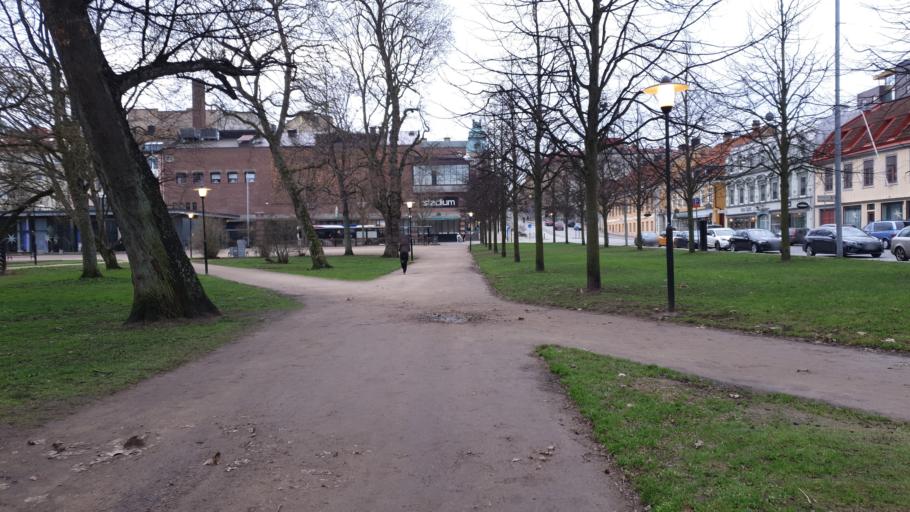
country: SE
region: Blekinge
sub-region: Karlskrona Kommun
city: Karlskrona
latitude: 56.1641
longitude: 15.5852
